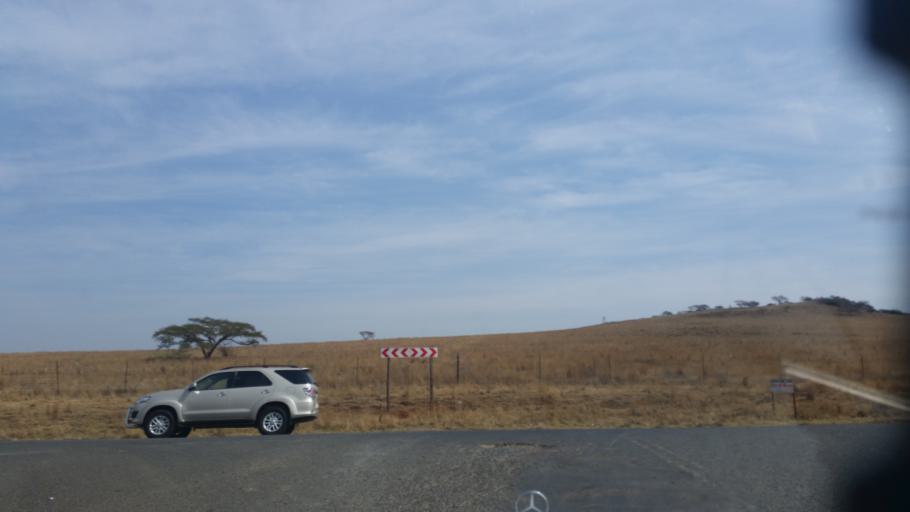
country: ZA
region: KwaZulu-Natal
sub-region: uThukela District Municipality
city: Estcourt
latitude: -29.0336
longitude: 29.9054
